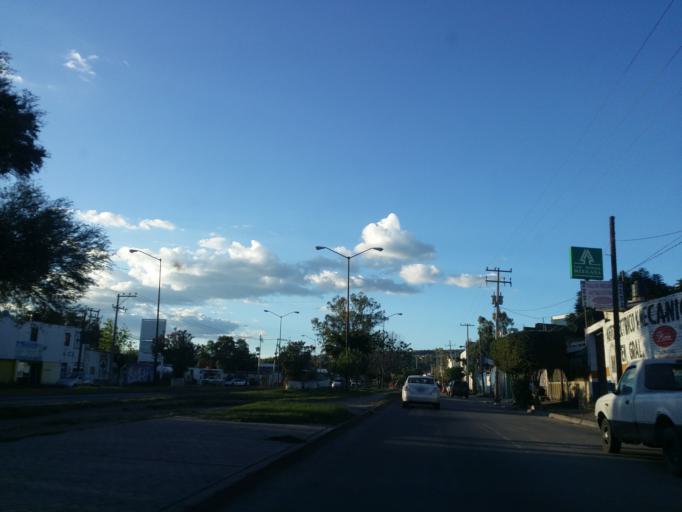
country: MX
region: Guanajuato
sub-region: Leon
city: Medina
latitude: 21.1915
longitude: -101.6652
